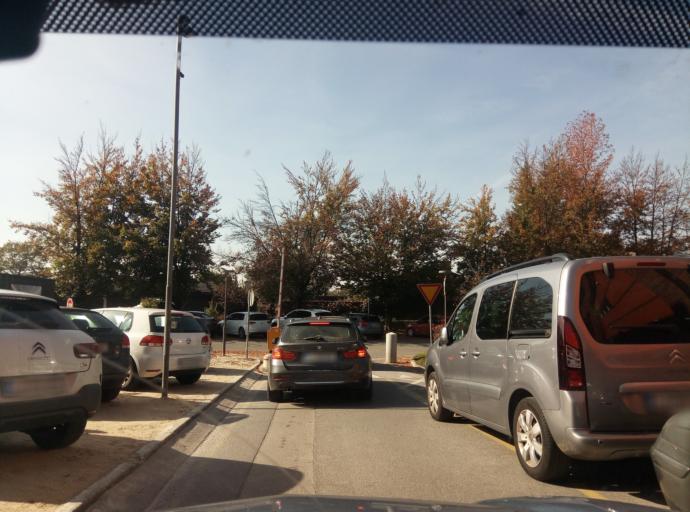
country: SI
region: Ljubljana
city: Ljubljana
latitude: 46.0358
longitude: 14.4891
